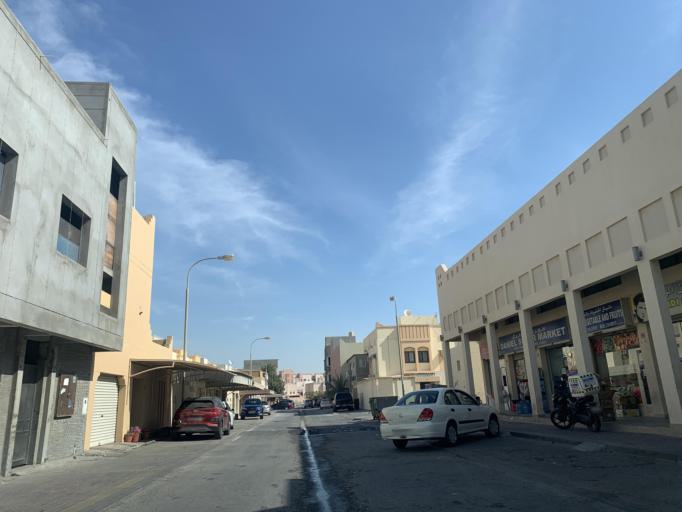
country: BH
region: Central Governorate
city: Madinat Hamad
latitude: 26.1164
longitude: 50.4858
